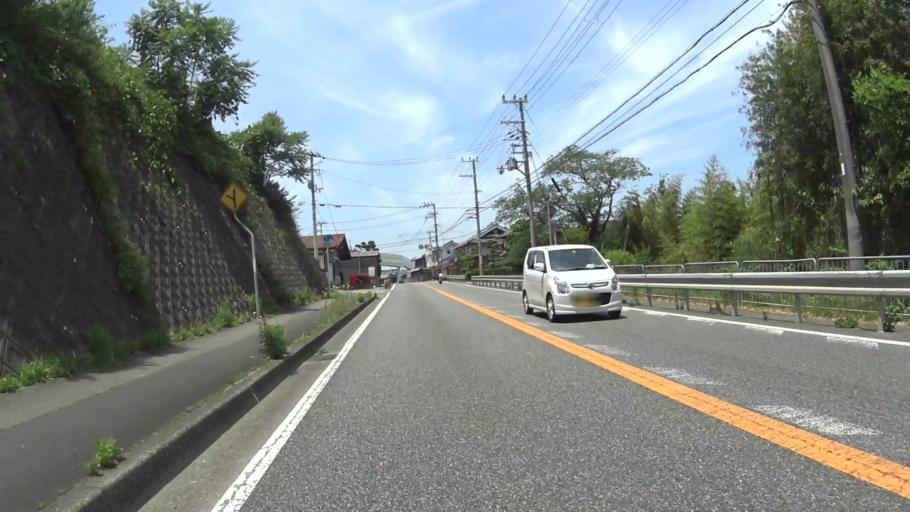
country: JP
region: Kyoto
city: Ayabe
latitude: 35.2152
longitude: 135.2370
